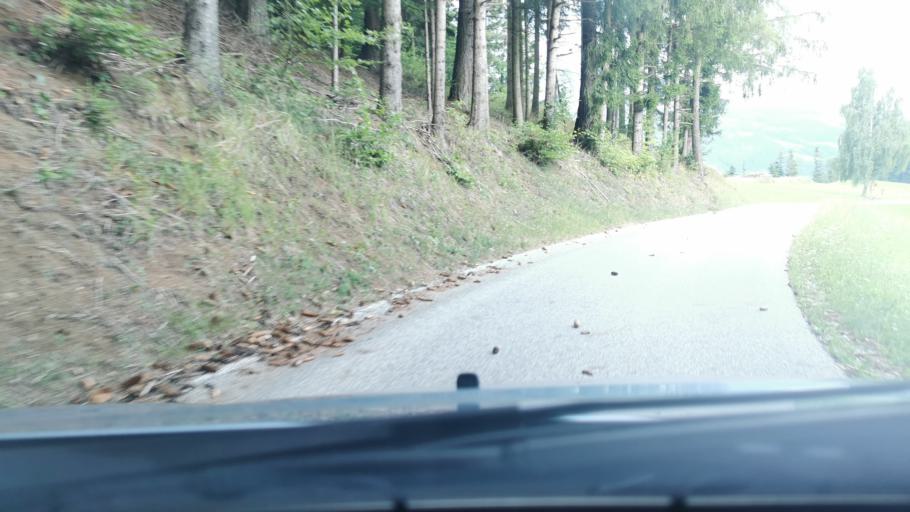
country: AT
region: Styria
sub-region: Politischer Bezirk Weiz
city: Koglhof
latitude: 47.3217
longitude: 15.6678
